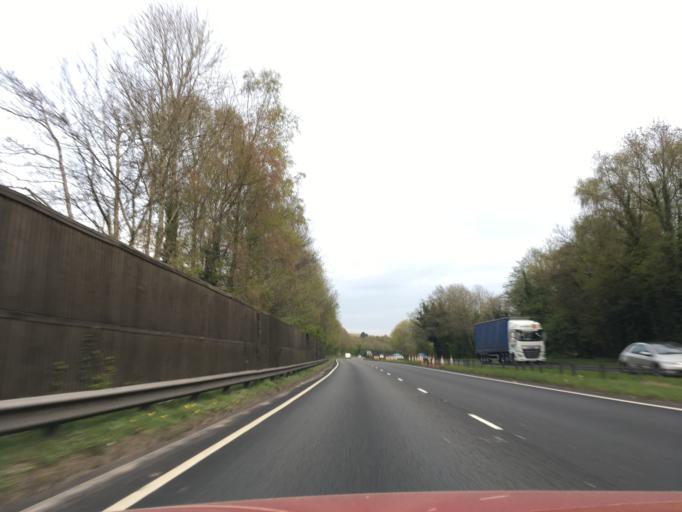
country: GB
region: Wales
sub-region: Caerphilly County Borough
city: Risca
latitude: 51.5929
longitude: -3.0701
